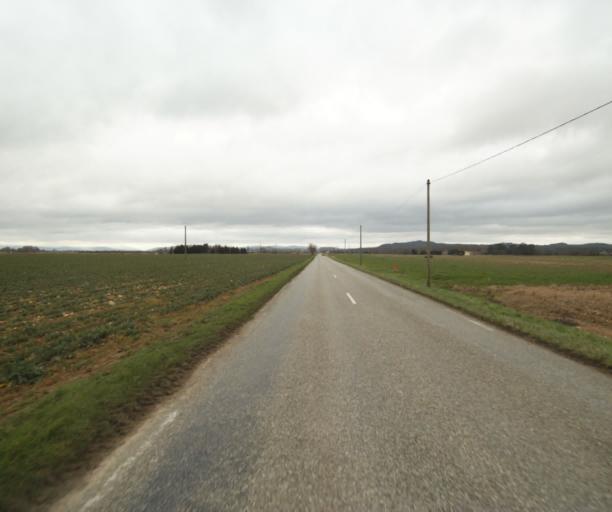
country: FR
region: Midi-Pyrenees
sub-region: Departement de l'Ariege
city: Saverdun
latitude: 43.2081
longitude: 1.6272
